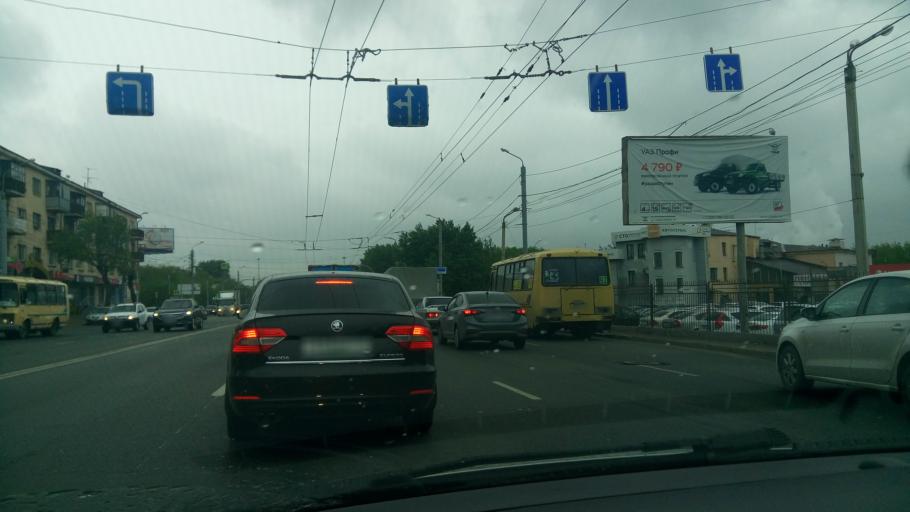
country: RU
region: Chelyabinsk
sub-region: Gorod Chelyabinsk
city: Chelyabinsk
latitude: 55.1907
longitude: 61.3865
